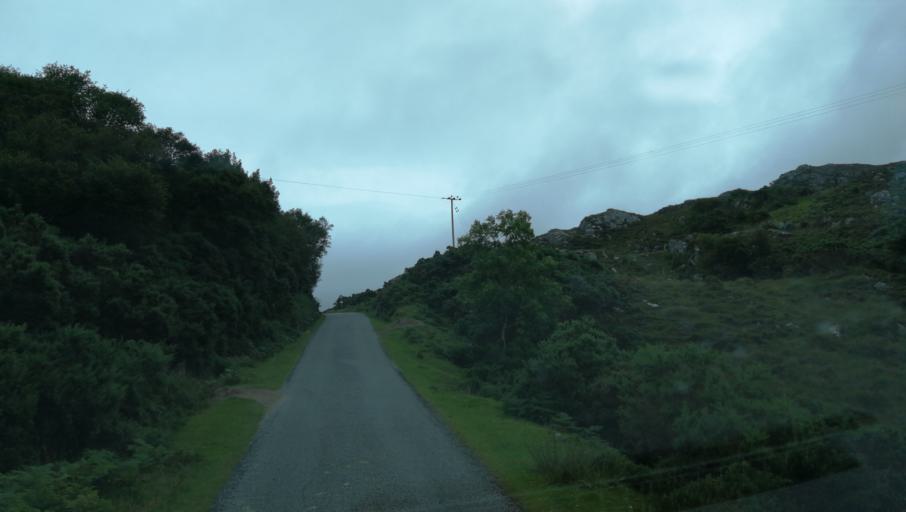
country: GB
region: Scotland
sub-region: Highland
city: Ullapool
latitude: 58.1383
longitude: -5.2444
